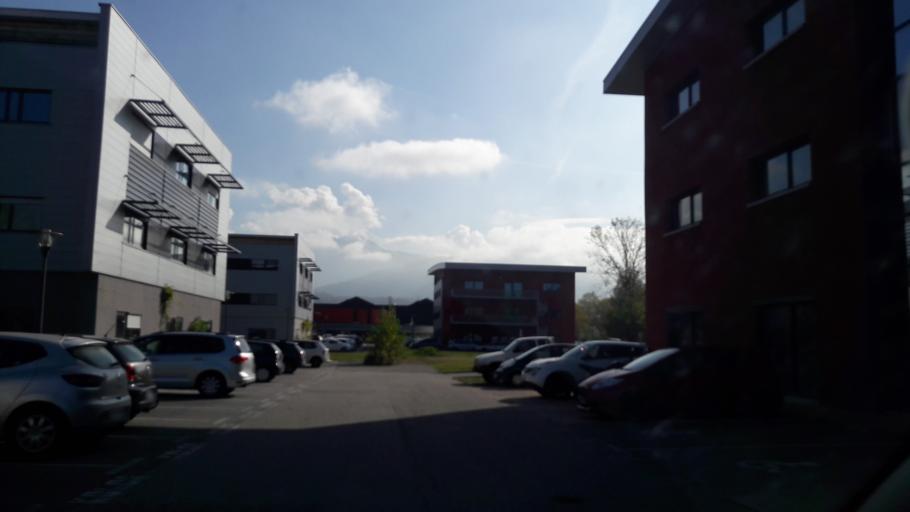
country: FR
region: Rhone-Alpes
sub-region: Departement de la Savoie
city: Montmelian
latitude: 45.4788
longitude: 6.0307
